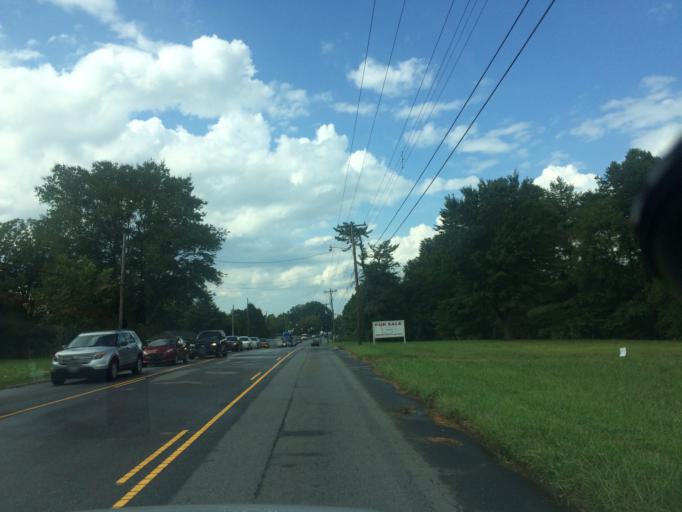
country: US
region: North Carolina
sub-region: Catawba County
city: Conover
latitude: 35.7066
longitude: -81.2633
